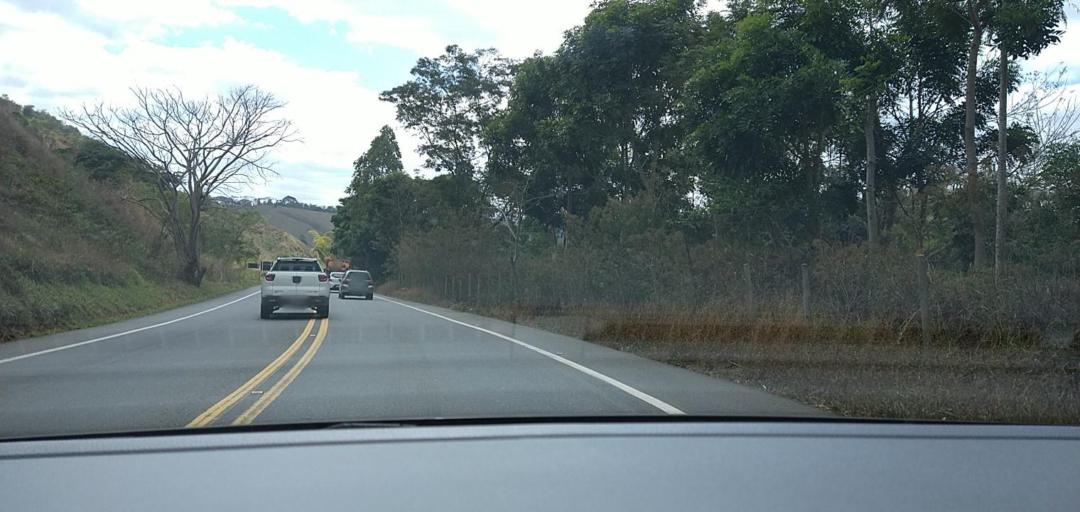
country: BR
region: Minas Gerais
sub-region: Ponte Nova
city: Ponte Nova
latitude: -20.5074
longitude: -42.8796
